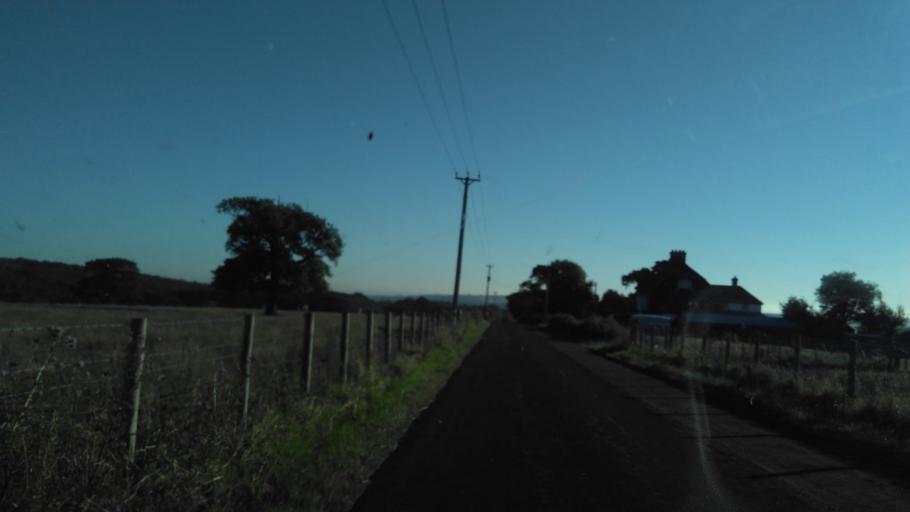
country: GB
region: England
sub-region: Kent
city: Dunkirk
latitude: 51.2992
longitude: 0.9835
